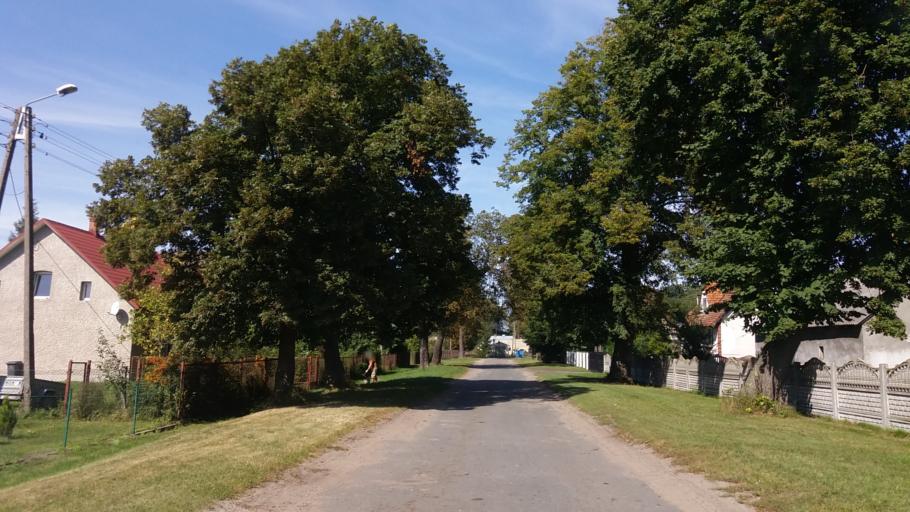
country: PL
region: West Pomeranian Voivodeship
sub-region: Powiat choszczenski
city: Choszczno
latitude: 53.1036
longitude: 15.4079
